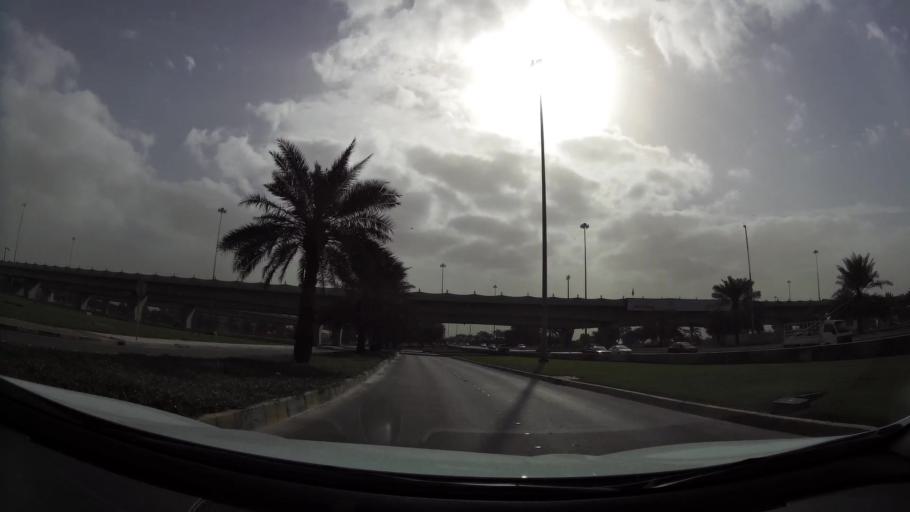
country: AE
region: Abu Dhabi
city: Abu Dhabi
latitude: 24.4064
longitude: 54.4764
